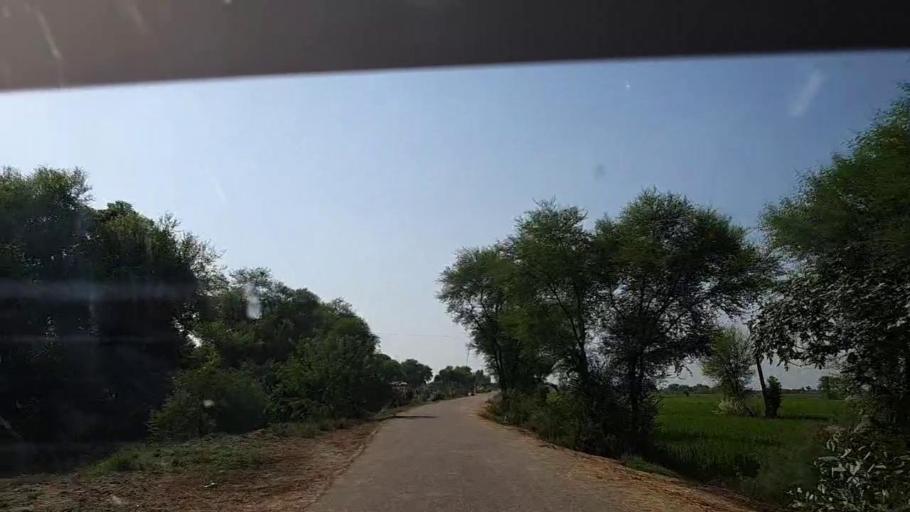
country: PK
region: Sindh
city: Tangwani
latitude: 28.2071
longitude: 69.0302
